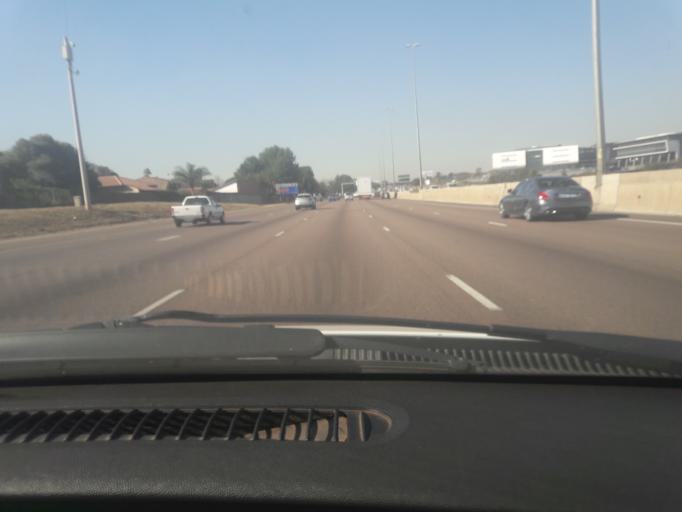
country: ZA
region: Gauteng
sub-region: City of Tshwane Metropolitan Municipality
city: Centurion
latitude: -25.8632
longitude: 28.2018
